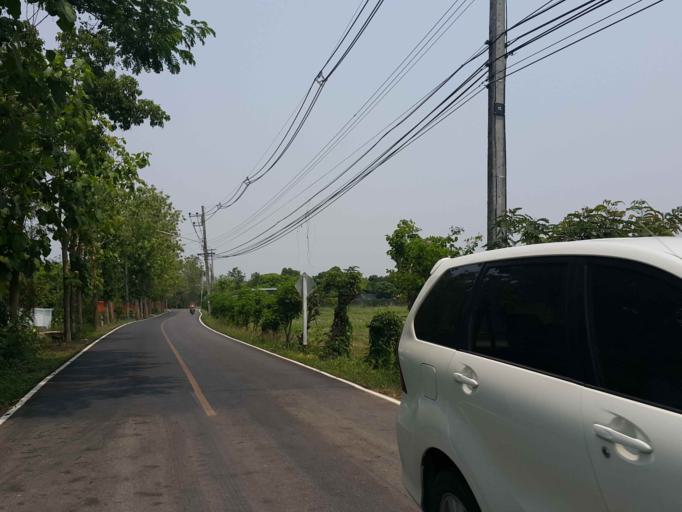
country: TH
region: Chiang Mai
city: San Sai
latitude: 18.8717
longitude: 99.0946
